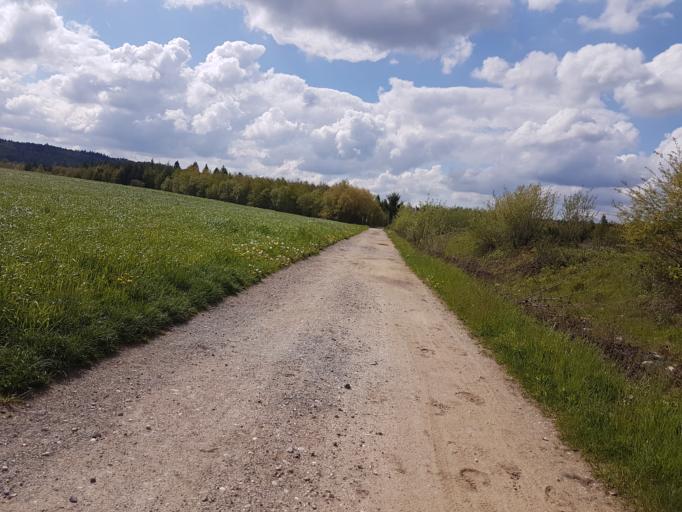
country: CH
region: Solothurn
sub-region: Bezirk Olten
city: Gunzgen
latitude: 47.3014
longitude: 7.8454
